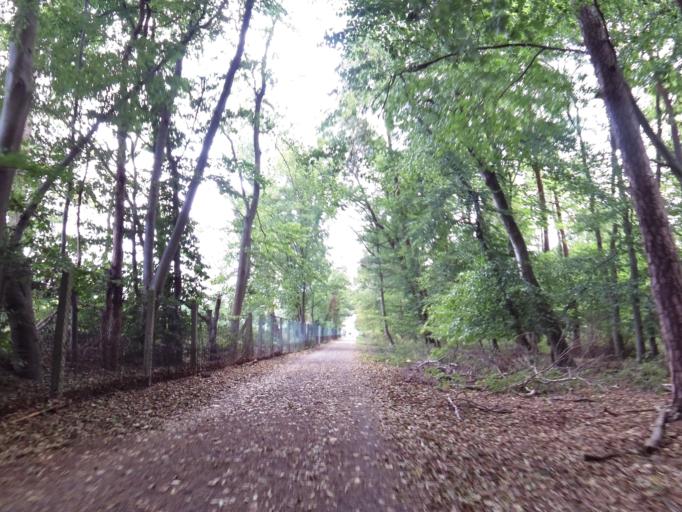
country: DE
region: Hesse
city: Morfelden-Walldorf
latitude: 50.0035
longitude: 8.5646
